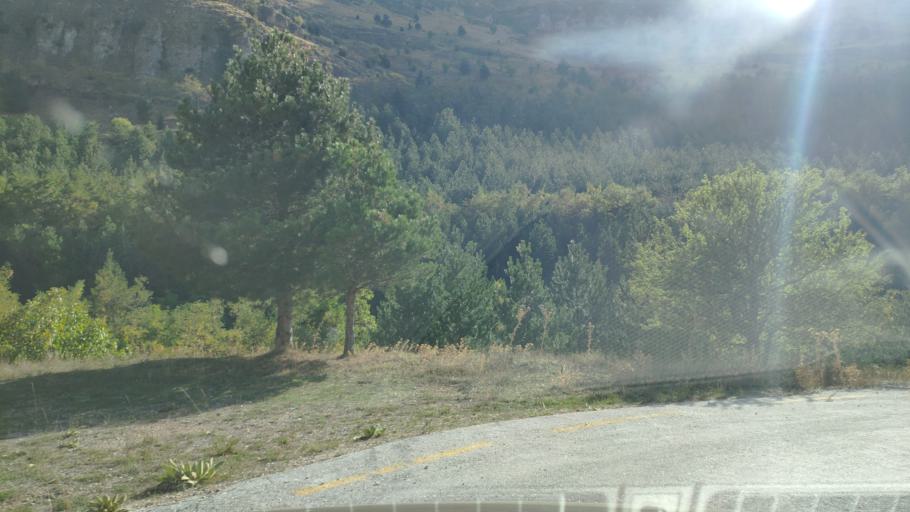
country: GR
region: West Greece
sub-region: Nomos Achaias
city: Aiyira
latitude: 38.0441
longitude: 22.3886
